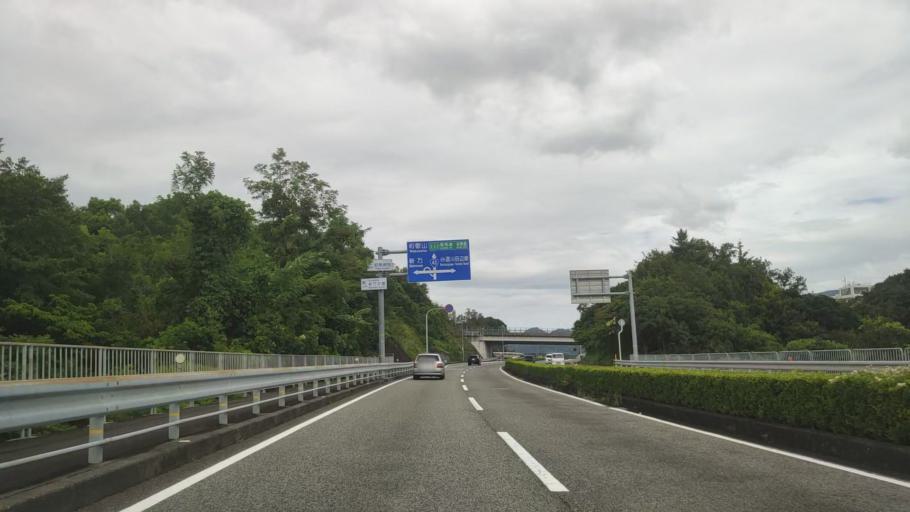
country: JP
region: Wakayama
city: Tanabe
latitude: 33.7303
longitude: 135.4005
